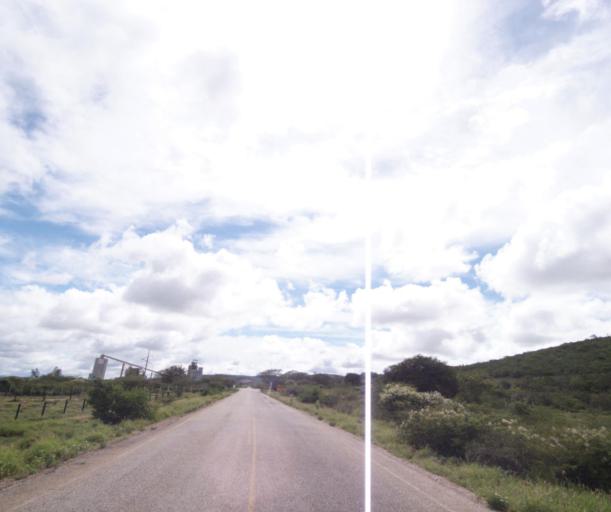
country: BR
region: Bahia
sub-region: Brumado
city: Brumado
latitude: -14.2001
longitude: -41.6040
